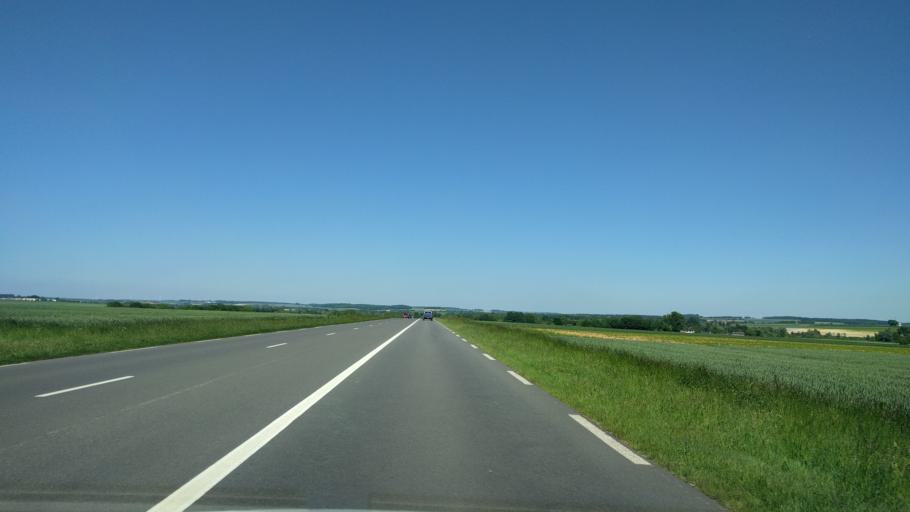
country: FR
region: Picardie
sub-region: Departement de la Somme
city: Peronne
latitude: 49.8859
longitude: 2.9090
